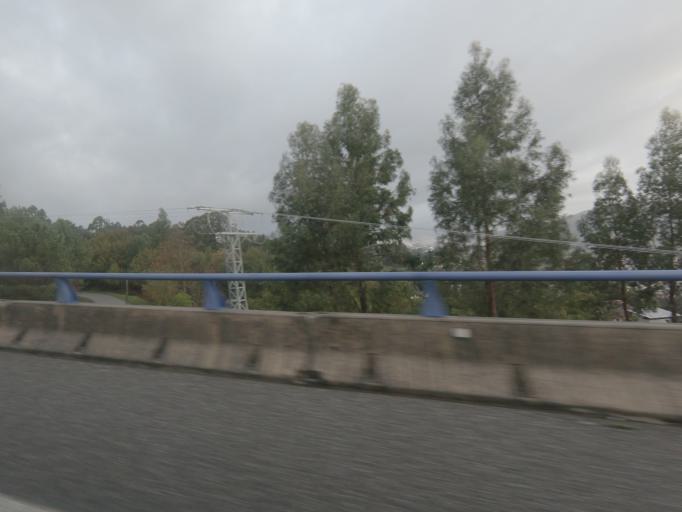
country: ES
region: Galicia
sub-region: Provincia de Pontevedra
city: Porrino
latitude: 42.1901
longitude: -8.6598
